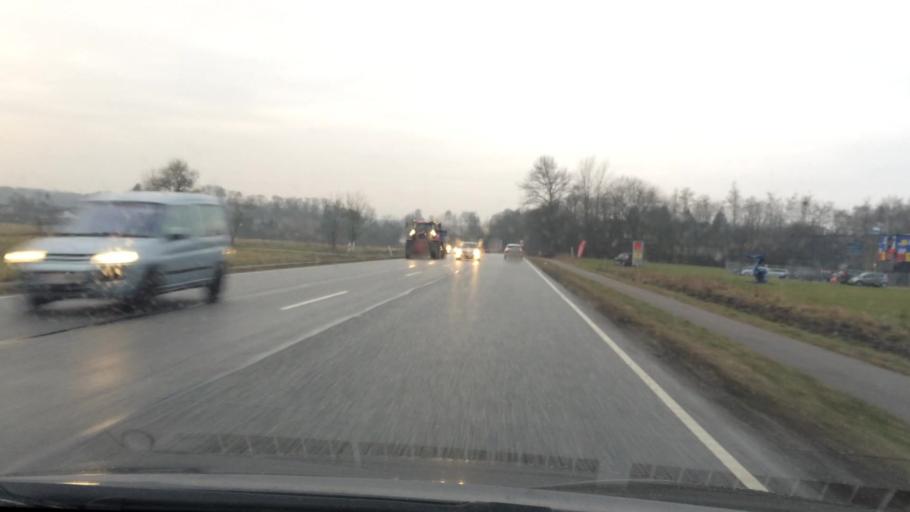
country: DK
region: Central Jutland
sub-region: Horsens Kommune
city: Horsens
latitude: 55.8242
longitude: 9.7944
